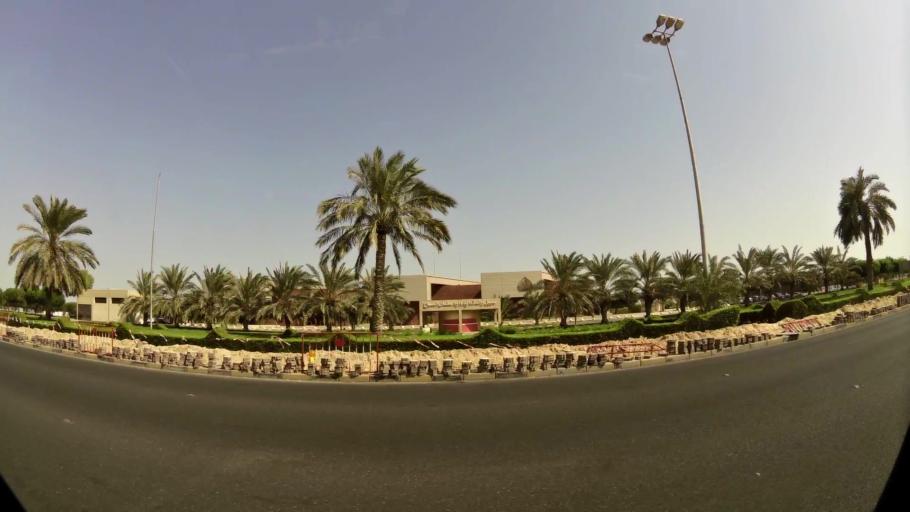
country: KW
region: Al Asimah
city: Ad Dasmah
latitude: 29.3630
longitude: 48.0227
